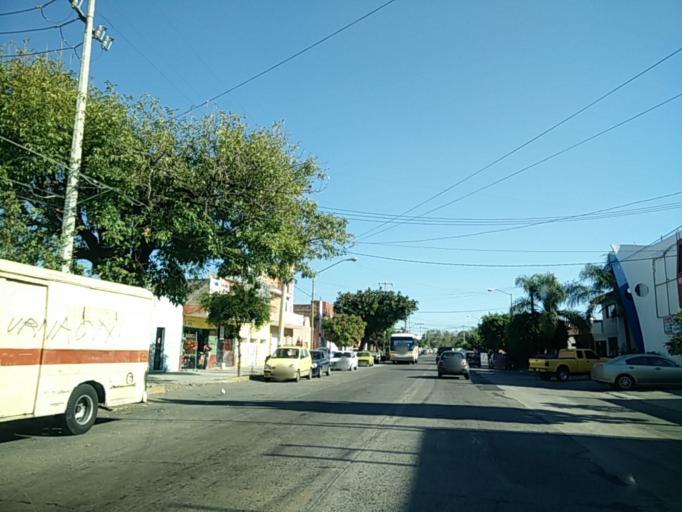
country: MX
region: Jalisco
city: Tlaquepaque
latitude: 20.6514
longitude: -103.3348
